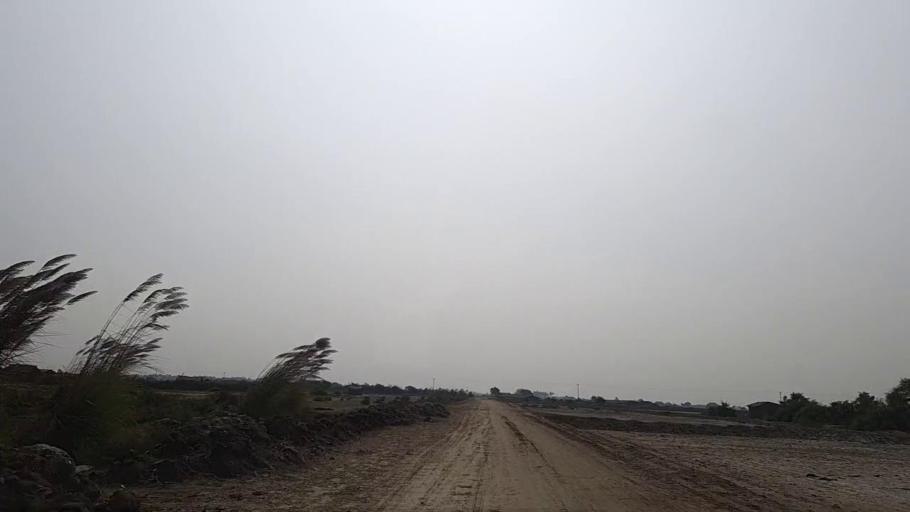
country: PK
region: Sindh
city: Mirpur Sakro
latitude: 24.6326
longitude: 67.7676
